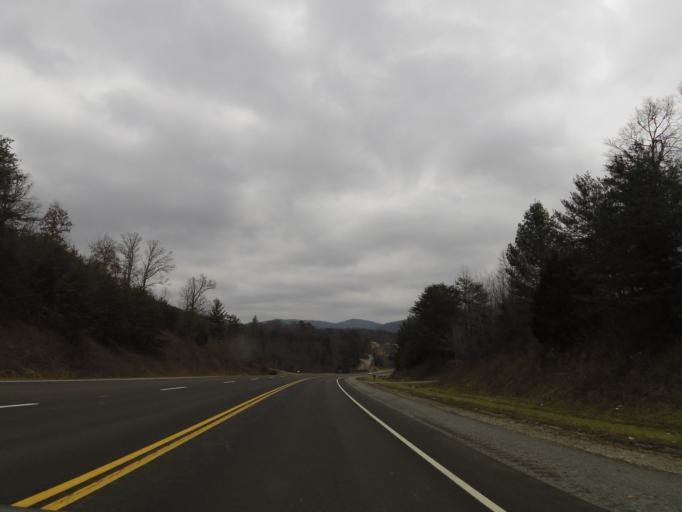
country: US
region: Tennessee
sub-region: Scott County
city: Huntsville
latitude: 36.3795
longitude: -84.3805
